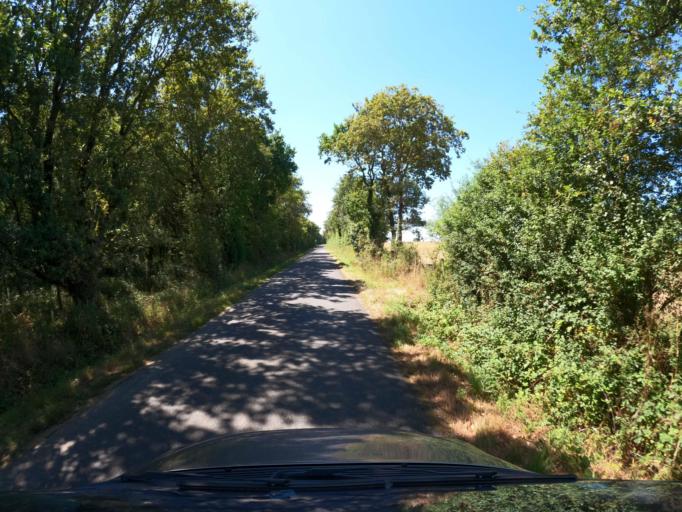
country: FR
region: Pays de la Loire
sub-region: Departement de la Loire-Atlantique
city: La Limouziniere
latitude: 46.9484
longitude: -1.6161
